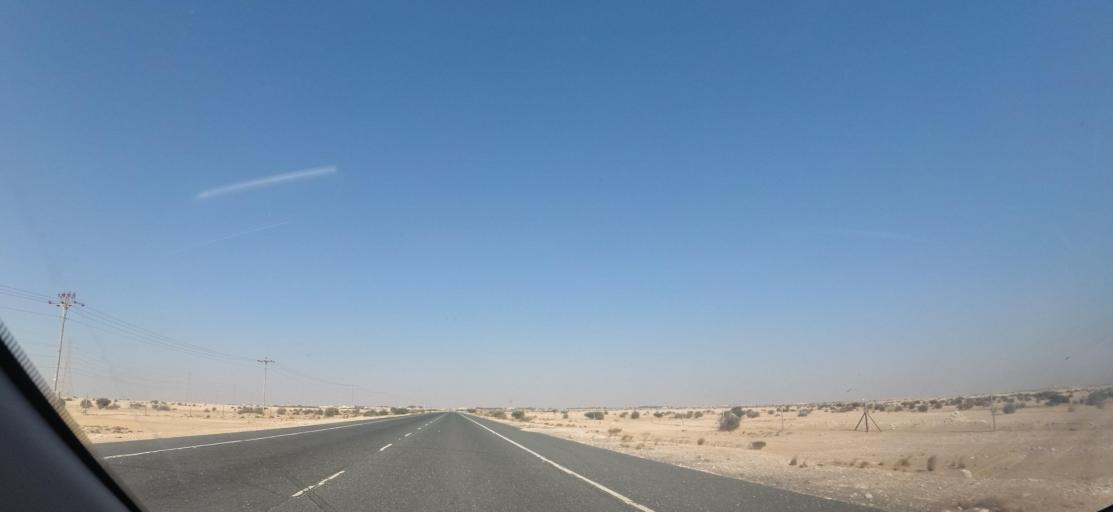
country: QA
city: Al Jumayliyah
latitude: 25.5954
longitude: 51.0678
